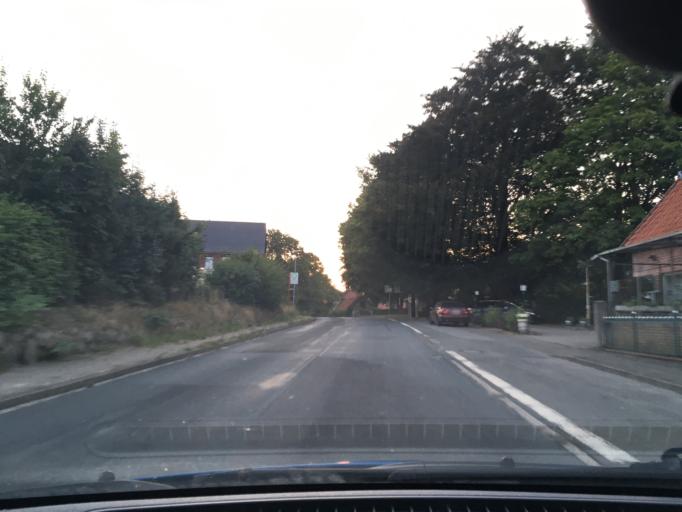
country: DE
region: Lower Saxony
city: Barnstedt
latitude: 53.1340
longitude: 10.3753
